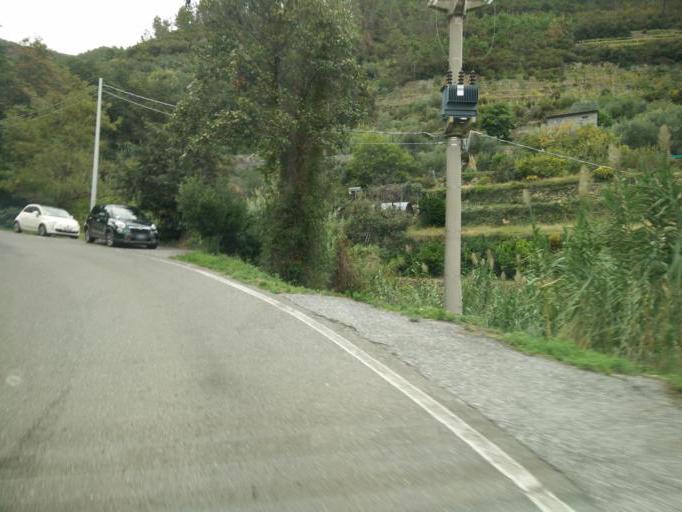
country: IT
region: Liguria
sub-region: Provincia di La Spezia
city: Riomaggiore
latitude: 44.1133
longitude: 9.7367
